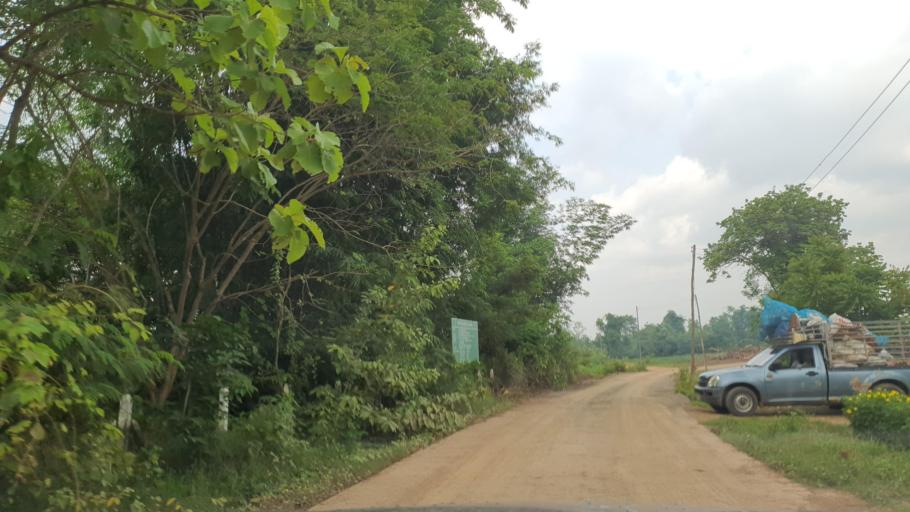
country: TH
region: Sukhothai
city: Thung Saliam
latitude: 17.2654
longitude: 99.5371
